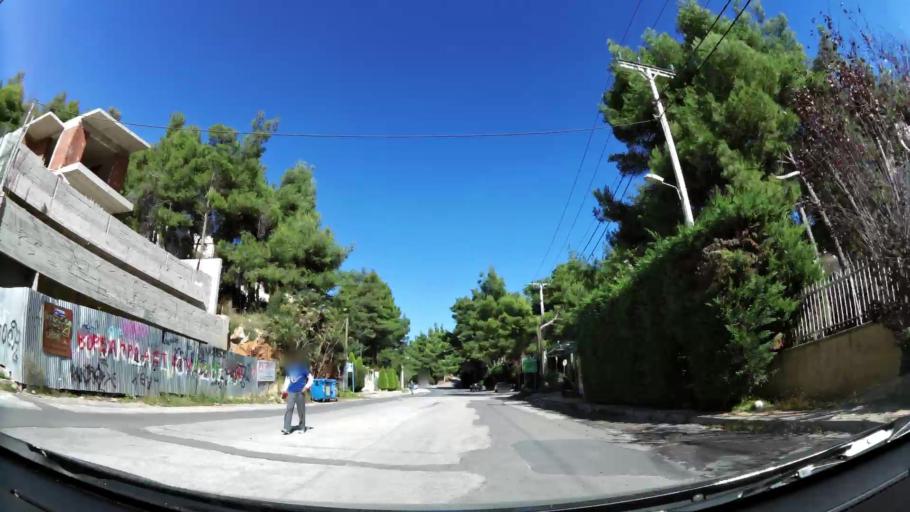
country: GR
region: Attica
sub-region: Nomarchia Anatolikis Attikis
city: Dionysos
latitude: 38.1036
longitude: 23.8843
